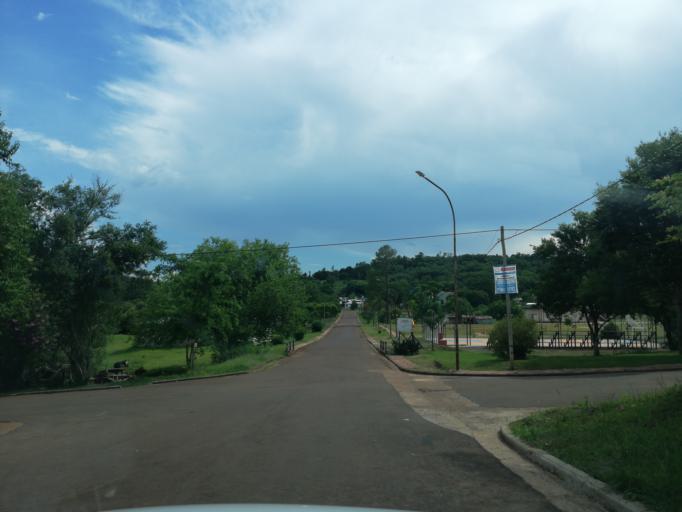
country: AR
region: Misiones
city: Cerro Azul
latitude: -27.5685
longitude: -55.5010
